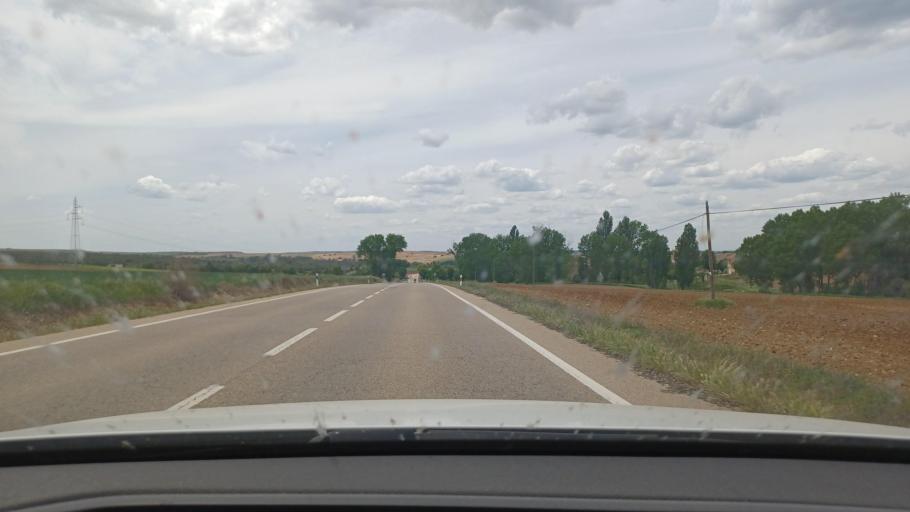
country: ES
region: Castille and Leon
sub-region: Provincia de Segovia
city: Castroserna de Abajo
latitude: 41.2406
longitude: -3.7371
